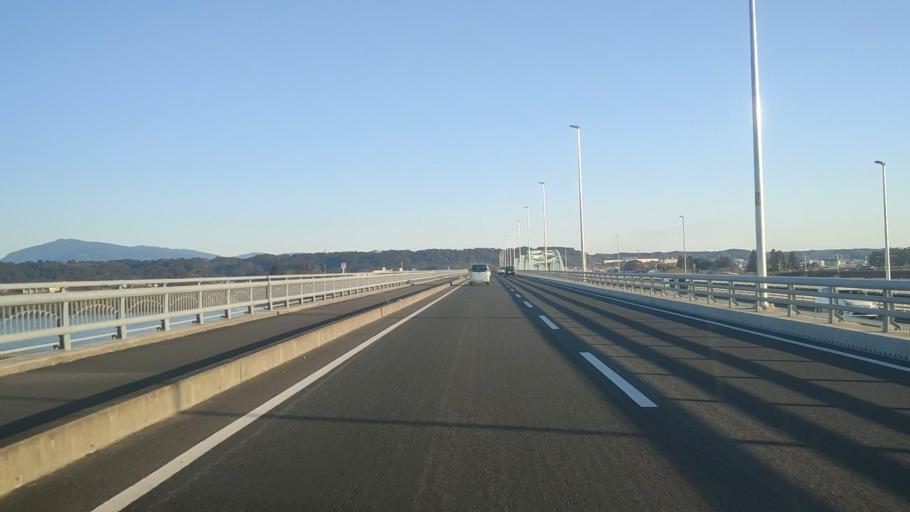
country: JP
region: Miyazaki
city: Tsuma
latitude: 32.0469
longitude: 131.4723
